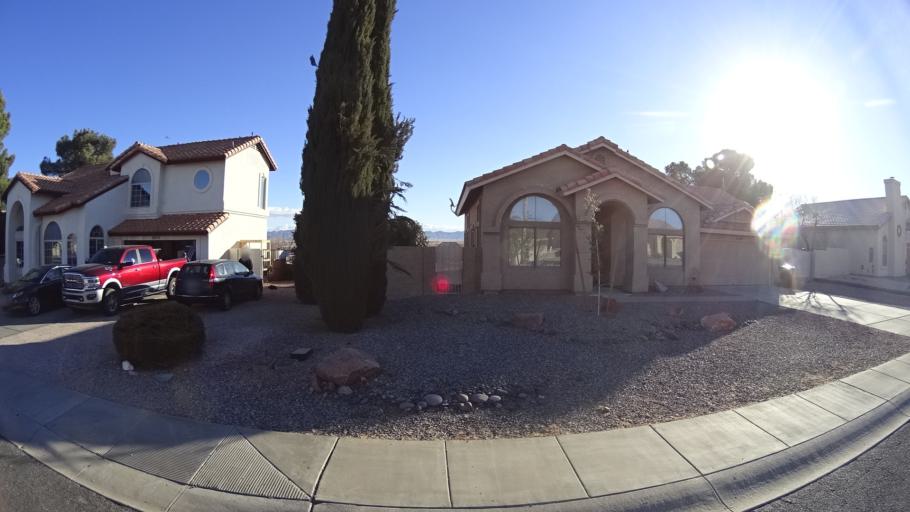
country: US
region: Arizona
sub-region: Mohave County
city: New Kingman-Butler
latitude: 35.2234
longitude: -113.9733
